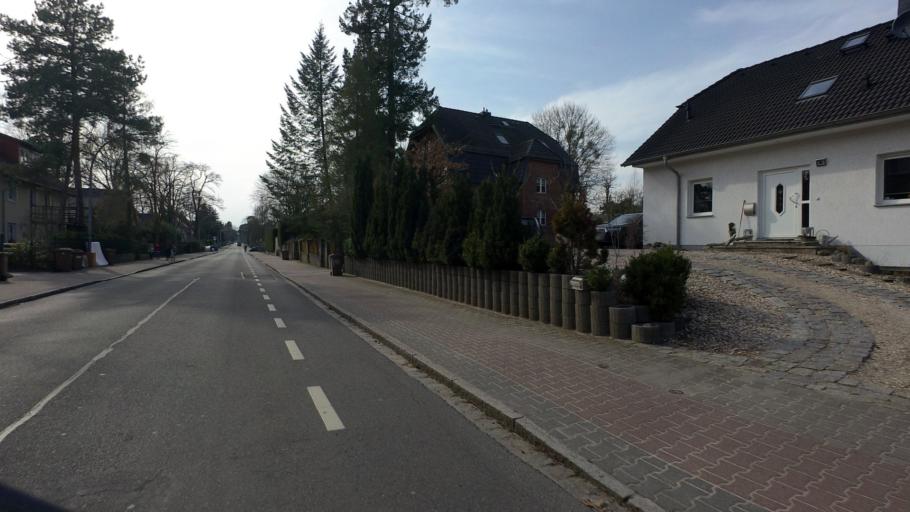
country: DE
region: Brandenburg
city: Kleinmachnow
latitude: 52.4142
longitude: 13.2286
